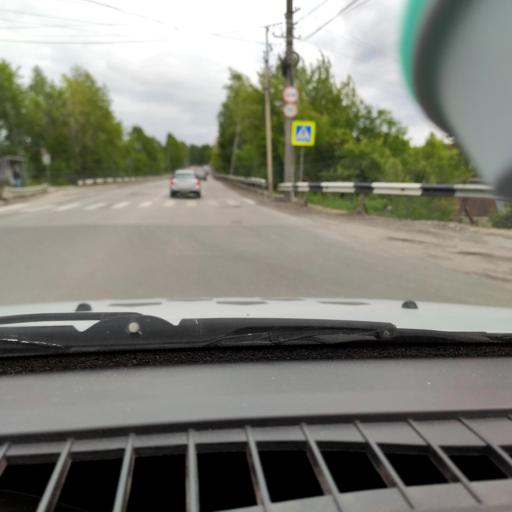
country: RU
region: Perm
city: Chusovoy
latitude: 58.2833
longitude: 57.8130
